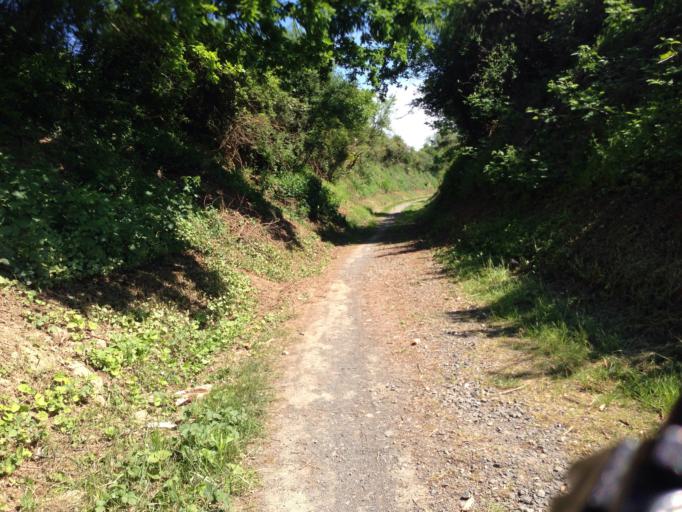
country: DE
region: Hesse
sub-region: Regierungsbezirk Darmstadt
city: Hammersbach
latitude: 50.2243
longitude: 8.9952
